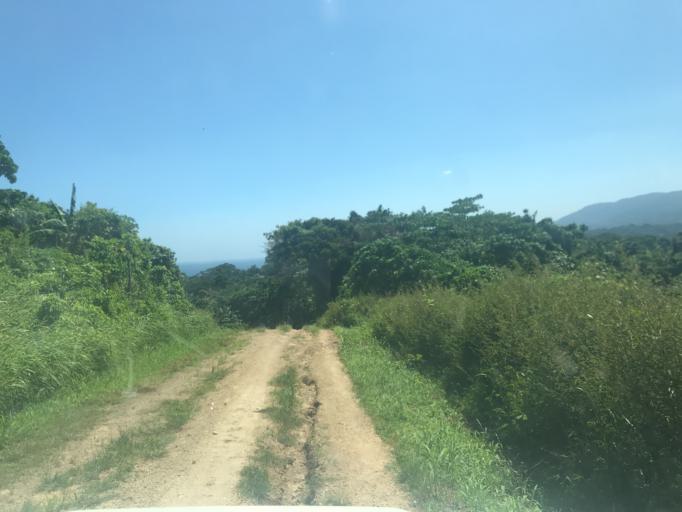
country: VU
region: Sanma
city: Luganville
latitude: -15.6348
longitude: 166.8007
